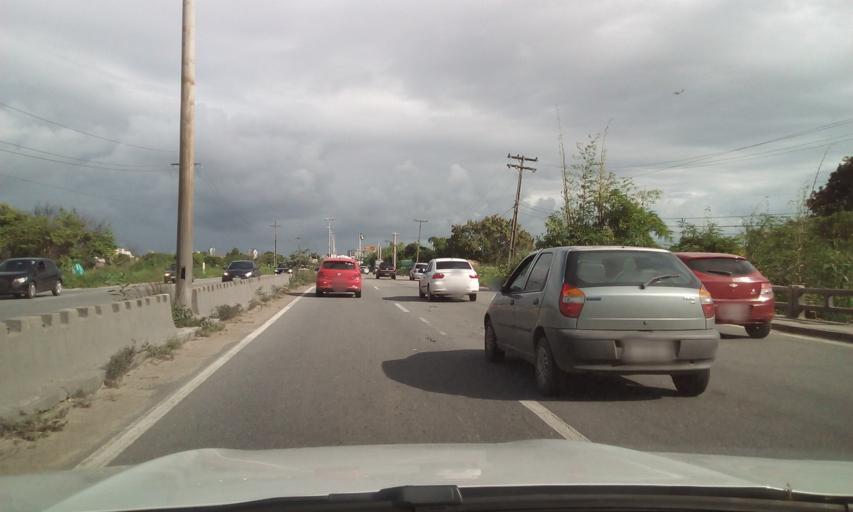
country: BR
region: Pernambuco
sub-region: Recife
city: Recife
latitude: -8.0230
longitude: -34.9428
